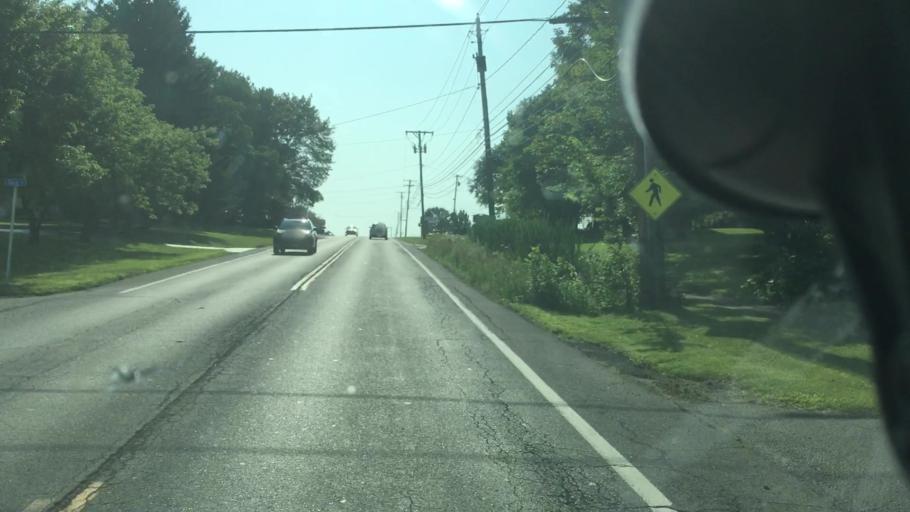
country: US
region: Ohio
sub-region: Mahoning County
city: Poland
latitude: 41.0237
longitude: -80.5968
